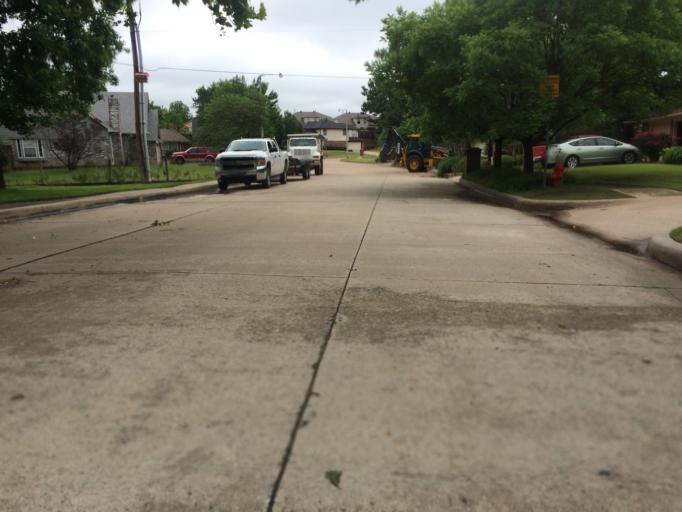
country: US
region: Oklahoma
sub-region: Cleveland County
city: Norman
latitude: 35.1835
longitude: -97.4550
